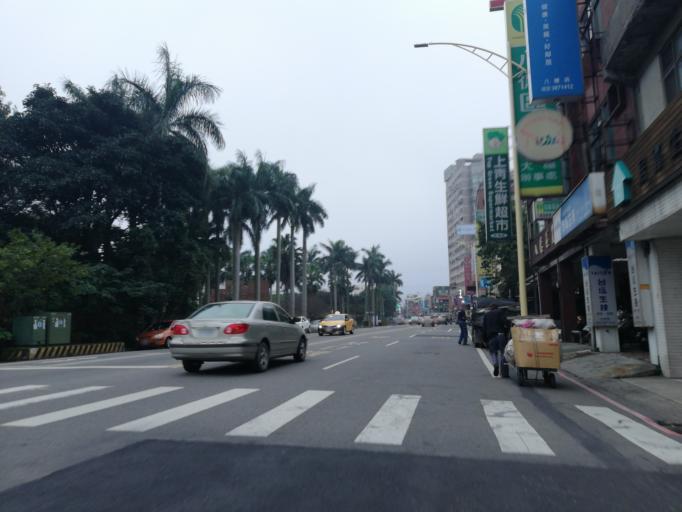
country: TW
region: Taiwan
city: Taoyuan City
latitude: 24.9726
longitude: 121.3020
